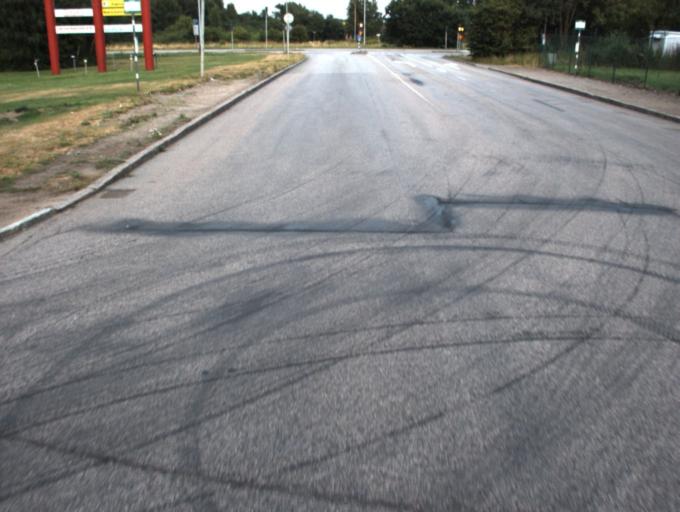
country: SE
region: Skane
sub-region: Helsingborg
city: Odakra
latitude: 56.0687
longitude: 12.7538
